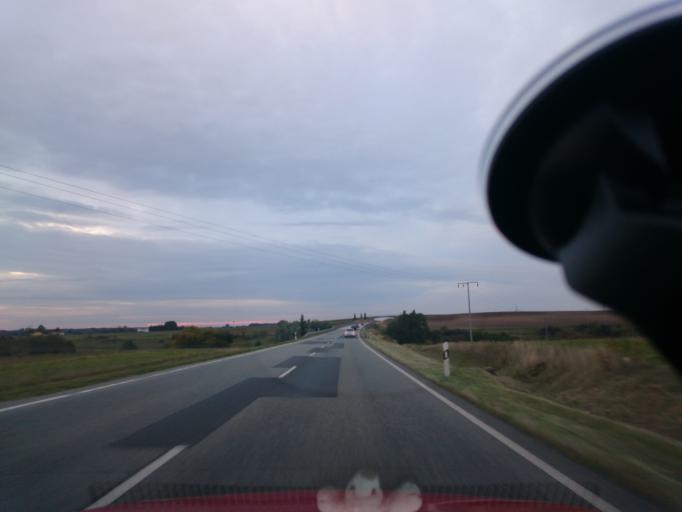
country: DE
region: Mecklenburg-Vorpommern
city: Ribnitz-Damgarten
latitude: 54.2292
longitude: 12.4239
